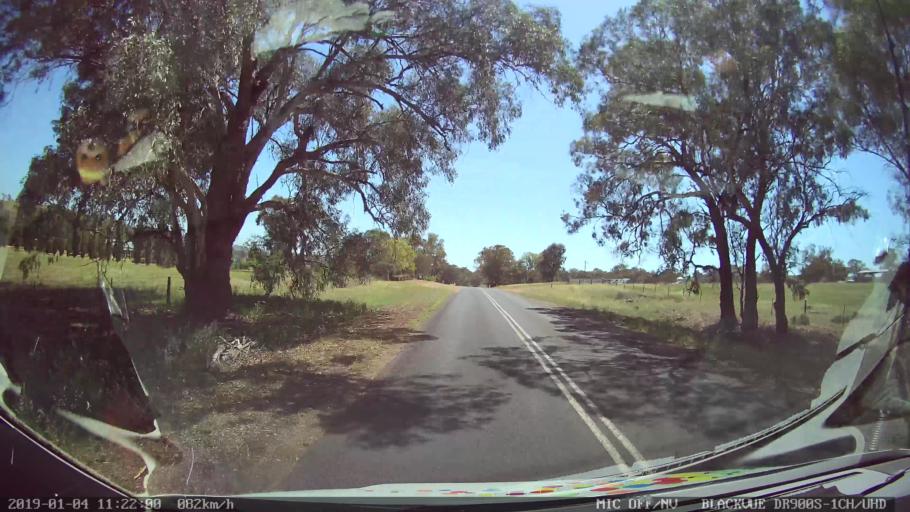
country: AU
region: New South Wales
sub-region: Cabonne
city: Molong
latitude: -33.1499
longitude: 148.7171
